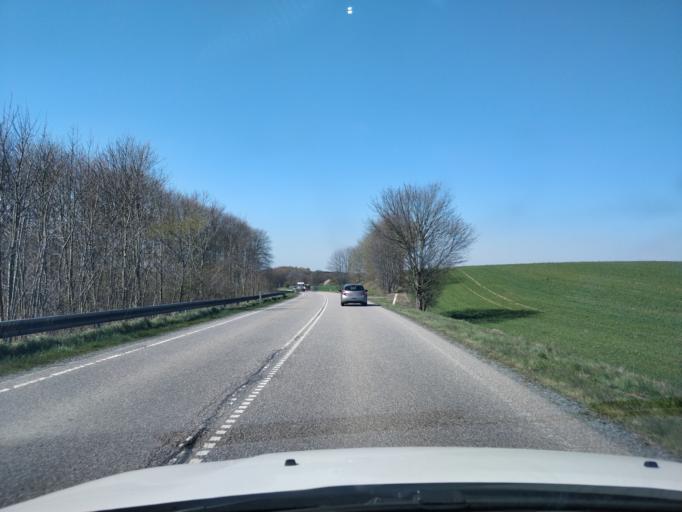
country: DK
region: Zealand
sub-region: Vordingborg Kommune
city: Nyrad
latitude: 55.0116
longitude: 11.9730
